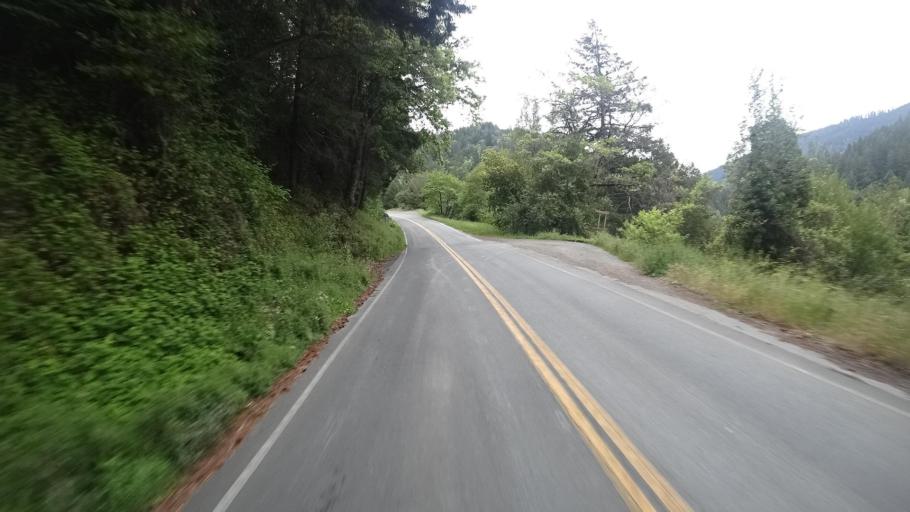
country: US
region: California
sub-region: Humboldt County
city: Willow Creek
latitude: 41.1868
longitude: -123.7065
